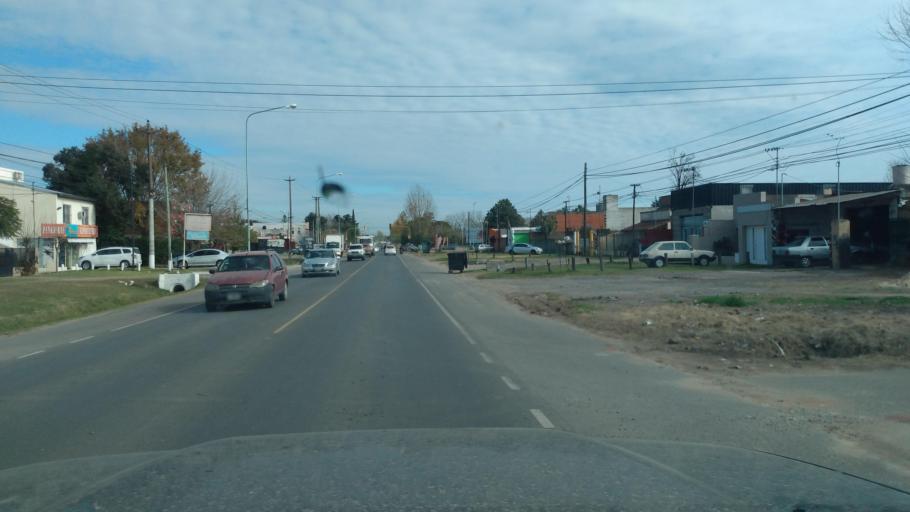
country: AR
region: Buenos Aires
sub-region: Partido de Lujan
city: Lujan
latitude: -34.5574
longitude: -59.1282
